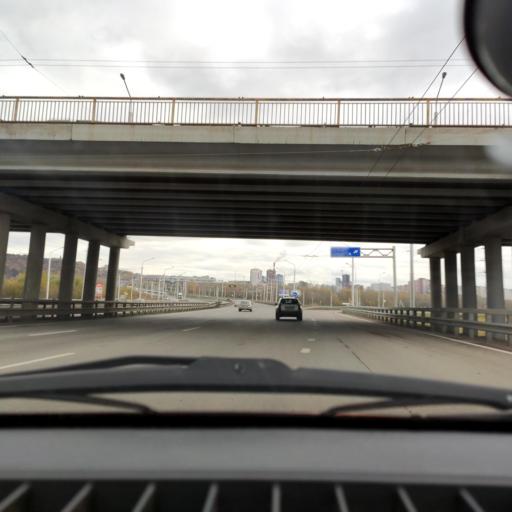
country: RU
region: Bashkortostan
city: Ufa
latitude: 54.7649
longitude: 55.9554
